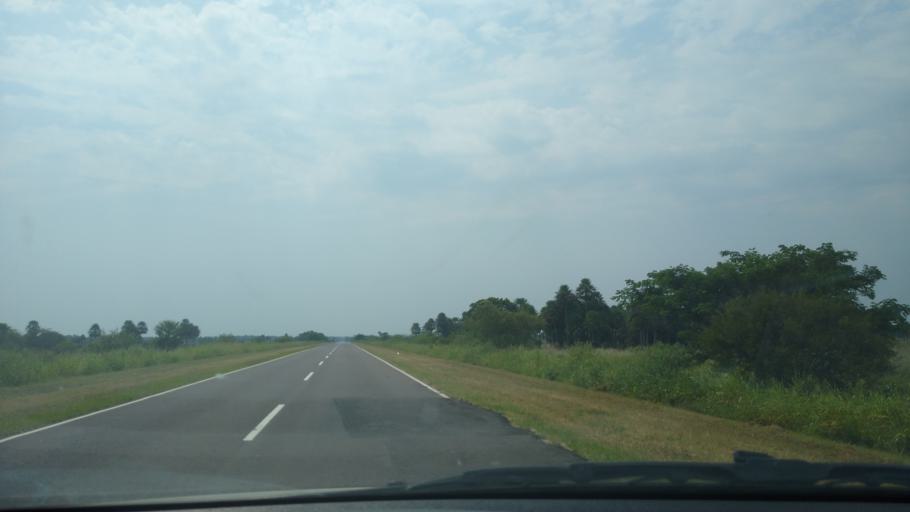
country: AR
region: Chaco
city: La Eduvigis
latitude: -26.9961
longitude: -58.9735
